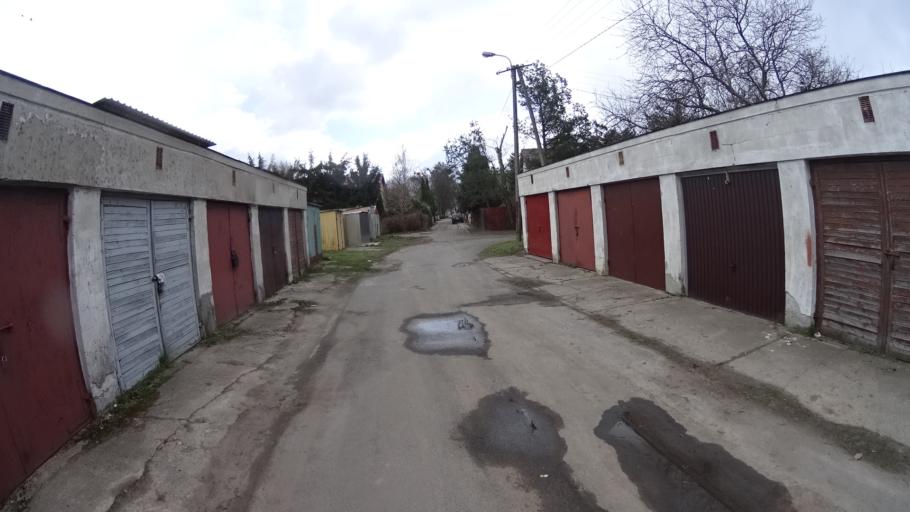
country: PL
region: Masovian Voivodeship
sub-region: Powiat warszawski zachodni
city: Blonie
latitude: 52.2184
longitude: 20.6479
